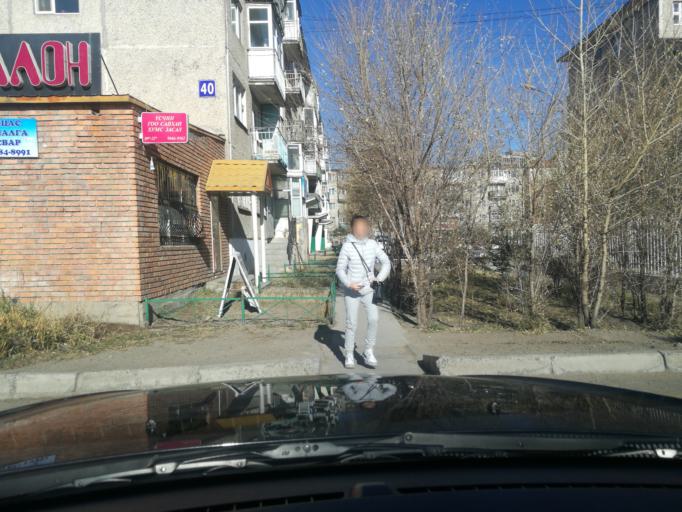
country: MN
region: Ulaanbaatar
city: Ulaanbaatar
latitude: 47.9030
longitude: 106.9067
